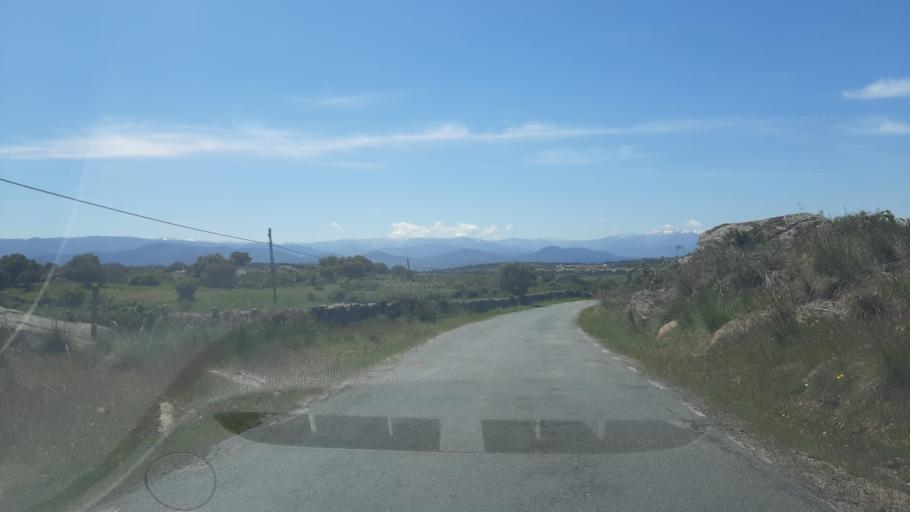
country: ES
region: Castille and Leon
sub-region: Provincia de Avila
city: Narrillos del Alamo
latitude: 40.5554
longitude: -5.4407
